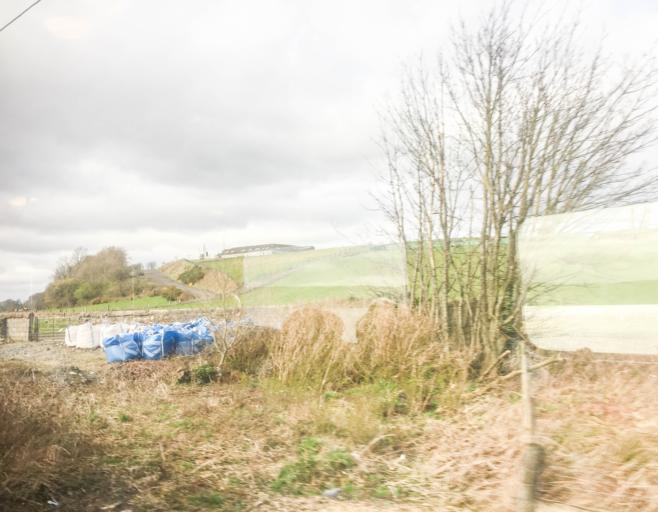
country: GB
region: Scotland
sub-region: Argyll and Bute
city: Cardross
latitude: 55.9520
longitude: -4.6272
